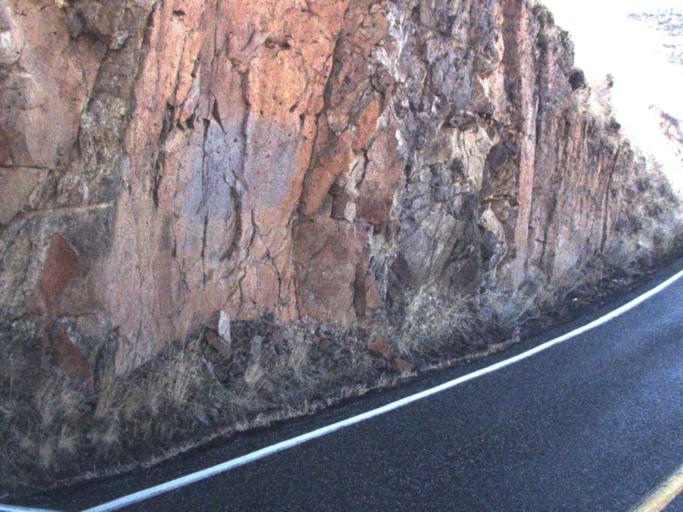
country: US
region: Washington
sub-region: Asotin County
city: Asotin
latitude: 46.0508
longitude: -117.2311
